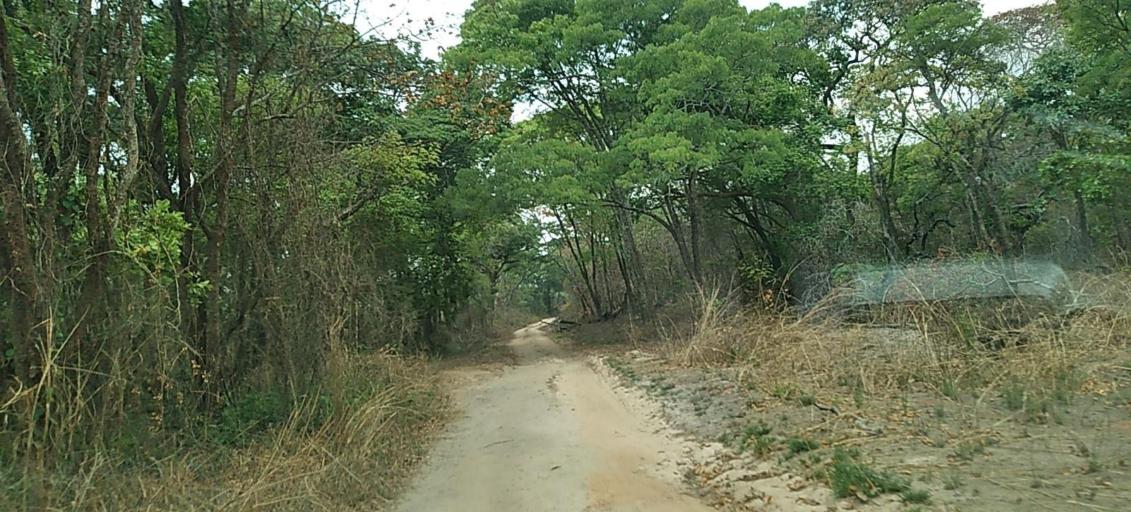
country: ZM
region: Copperbelt
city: Chingola
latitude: -12.7556
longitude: 27.7084
